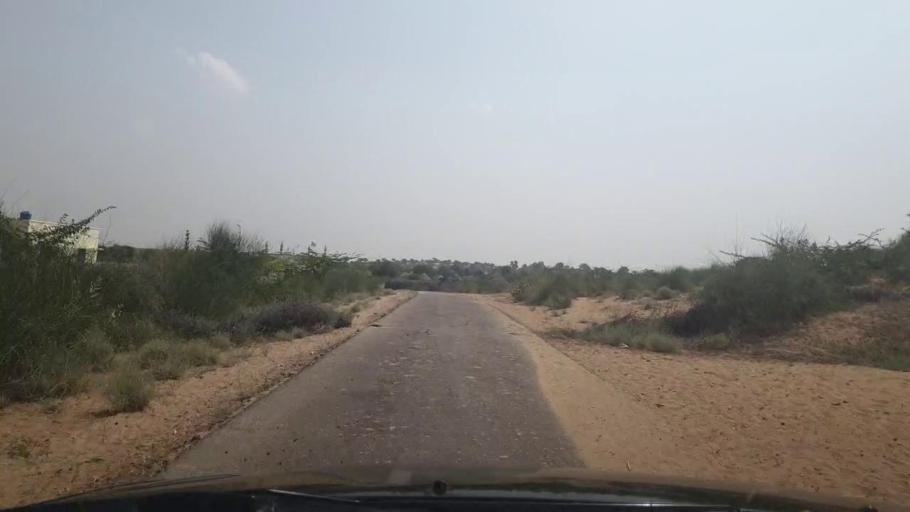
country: PK
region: Sindh
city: Islamkot
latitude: 25.0088
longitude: 70.4075
